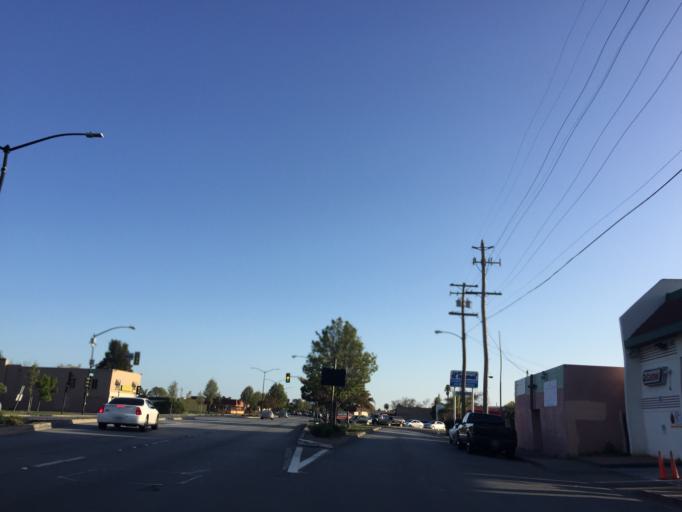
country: US
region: California
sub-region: Contra Costa County
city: San Pablo
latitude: 37.9699
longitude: -122.3438
